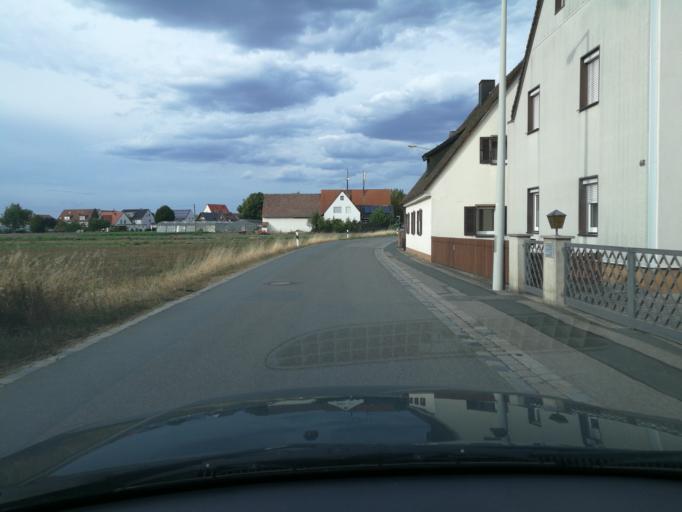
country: DE
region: Bavaria
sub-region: Regierungsbezirk Mittelfranken
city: Wetzendorf
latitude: 49.4885
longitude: 11.0612
